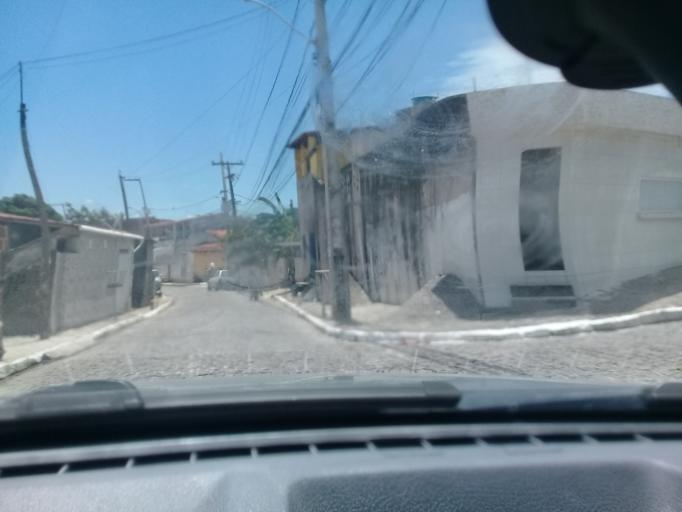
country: BR
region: Pernambuco
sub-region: Jaboatao Dos Guararapes
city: Jaboatao dos Guararapes
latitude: -8.1258
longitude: -34.9532
